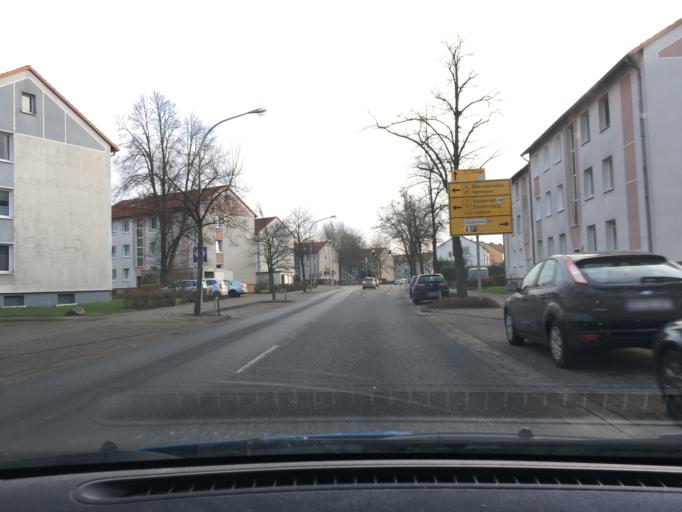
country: DE
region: Lower Saxony
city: Uelzen
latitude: 52.9649
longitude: 10.5751
